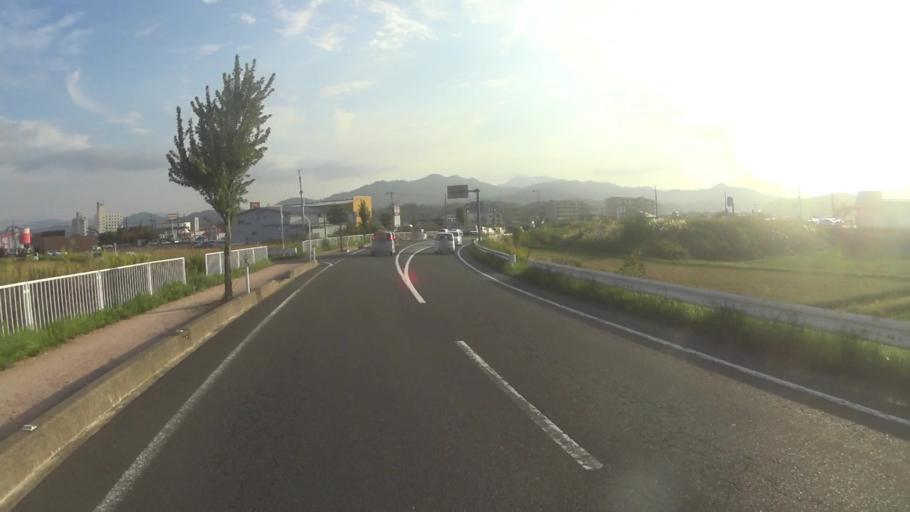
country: JP
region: Kyoto
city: Miyazu
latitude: 35.6109
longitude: 135.0802
